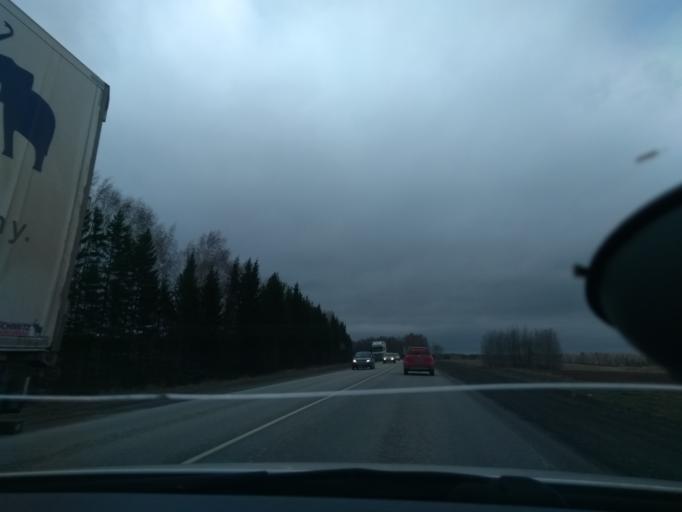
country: RU
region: Perm
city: Kungur
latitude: 57.4758
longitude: 56.7358
